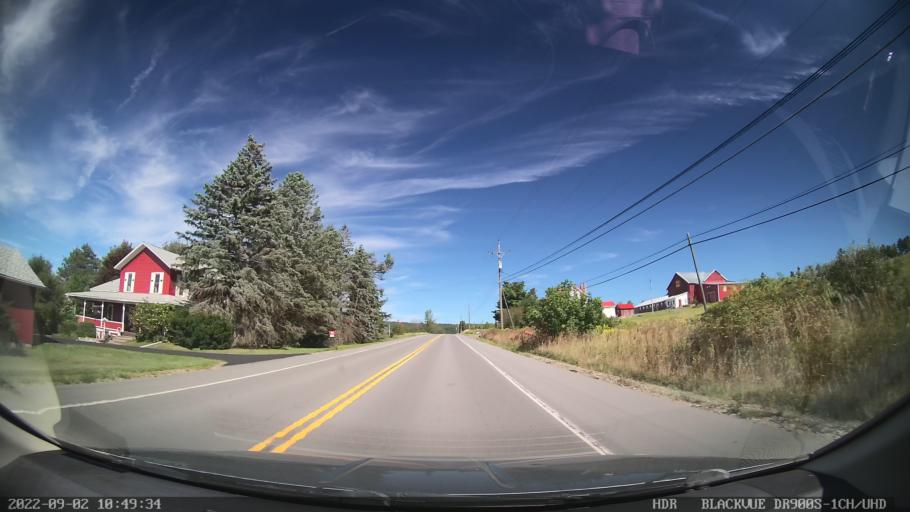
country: US
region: Pennsylvania
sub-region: Tioga County
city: Blossburg
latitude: 41.6021
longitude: -77.1124
